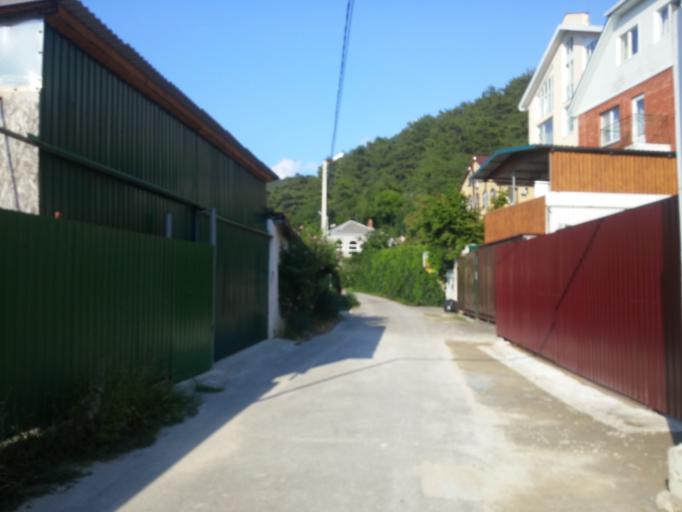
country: RU
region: Krasnodarskiy
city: Divnomorskoye
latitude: 44.4649
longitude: 38.1602
